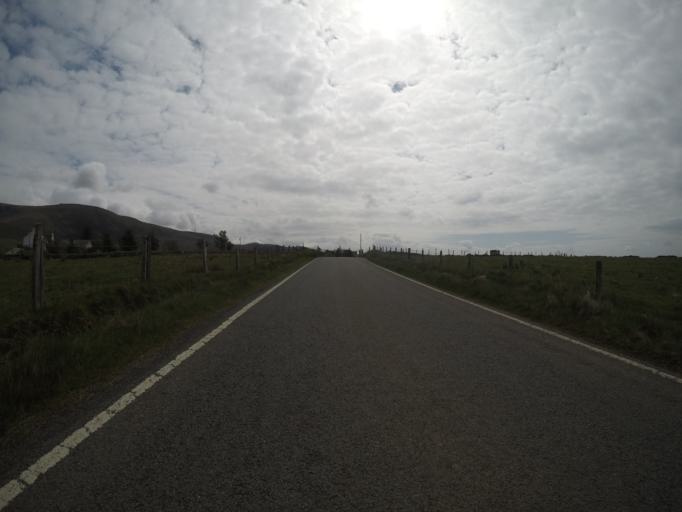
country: GB
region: Scotland
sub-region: Highland
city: Portree
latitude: 57.6418
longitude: -6.3767
